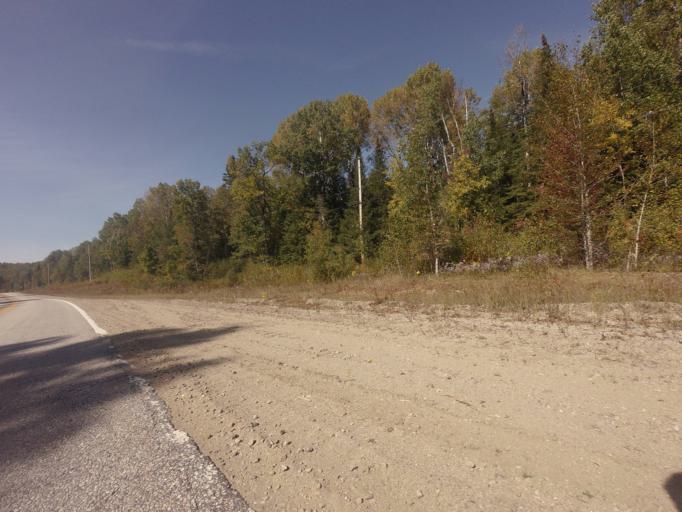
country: CA
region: Quebec
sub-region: Outaouais
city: Maniwaki
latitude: 46.5561
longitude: -75.7827
